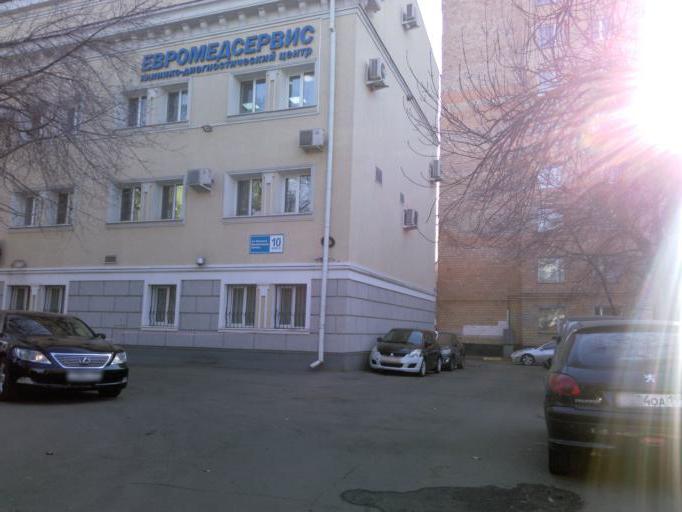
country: RU
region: Moscow
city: Novyye Cheremushki
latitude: 55.7079
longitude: 37.6011
